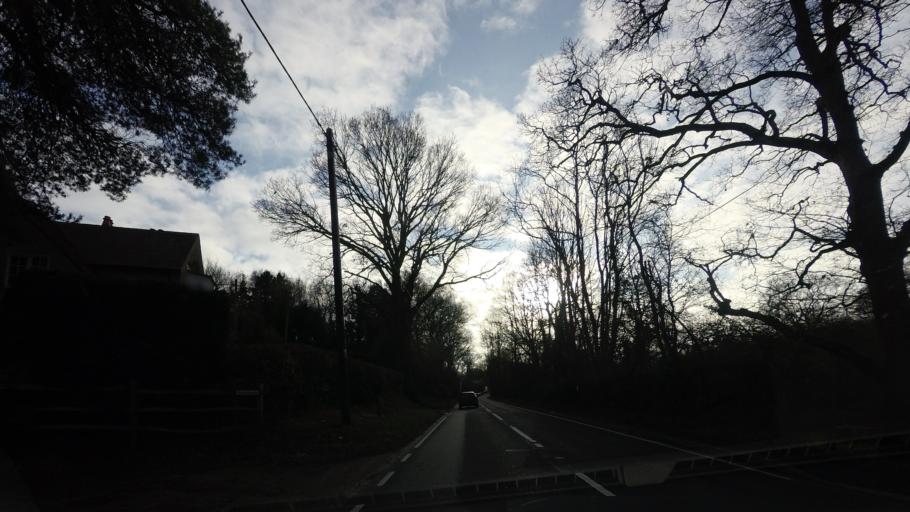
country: GB
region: England
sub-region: East Sussex
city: Battle
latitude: 50.9323
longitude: 0.4819
